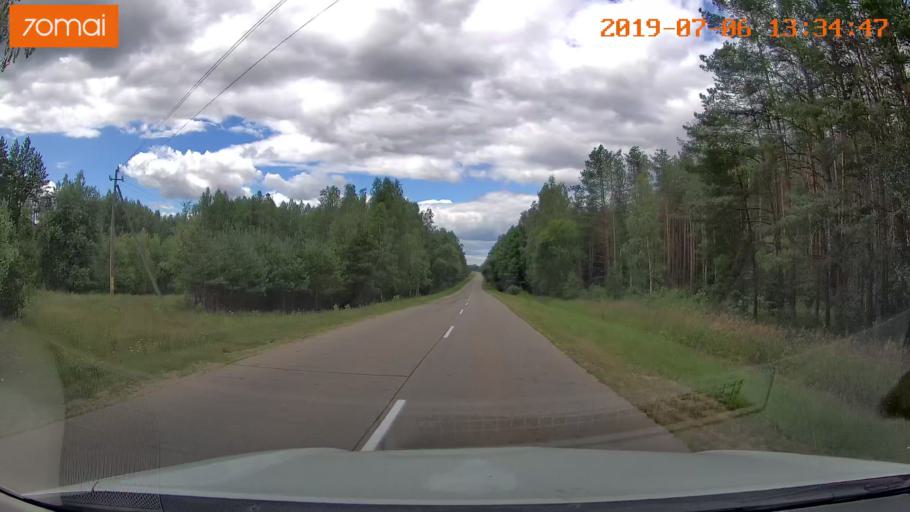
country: BY
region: Minsk
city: Enyerhyetykaw
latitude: 53.6772
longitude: 26.8924
